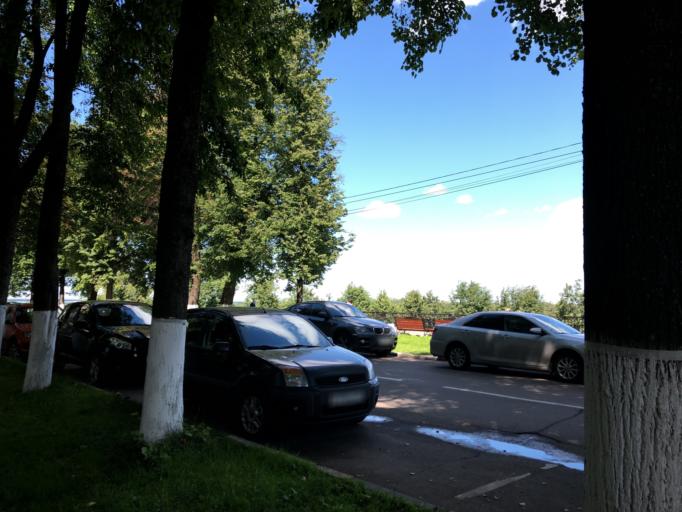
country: RU
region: Jaroslavl
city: Yaroslavl
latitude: 57.6307
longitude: 39.8951
